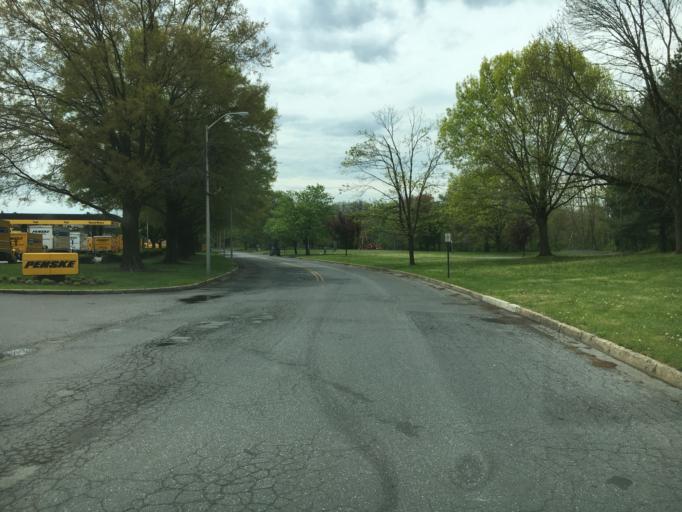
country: US
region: Pennsylvania
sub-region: Berks County
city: West Reading
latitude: 40.3326
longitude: -75.9373
